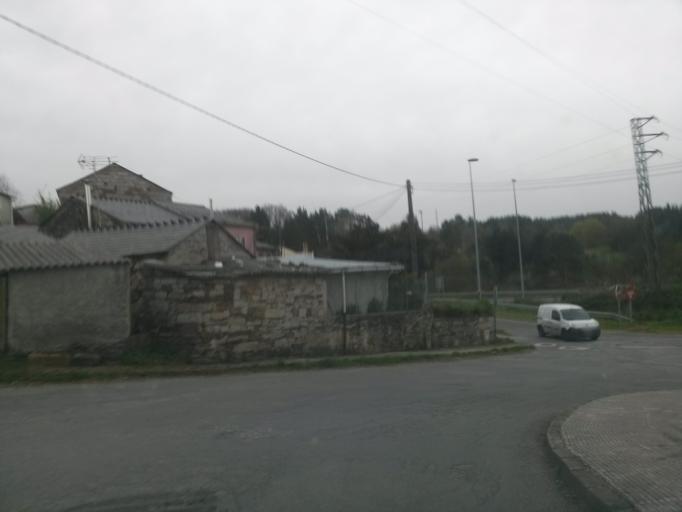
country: ES
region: Galicia
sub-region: Provincia de Lugo
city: Lugo
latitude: 43.0293
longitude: -7.5421
